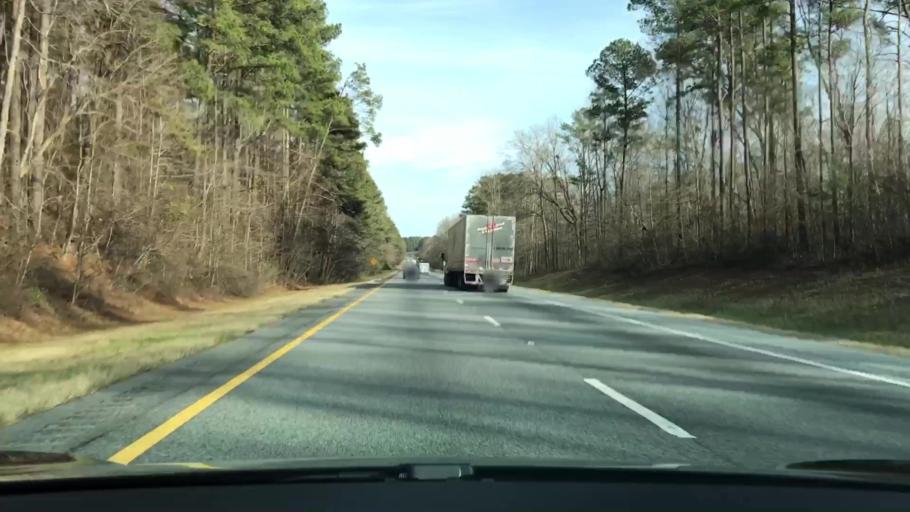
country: US
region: Georgia
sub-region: Morgan County
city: Madison
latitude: 33.5763
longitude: -83.5553
